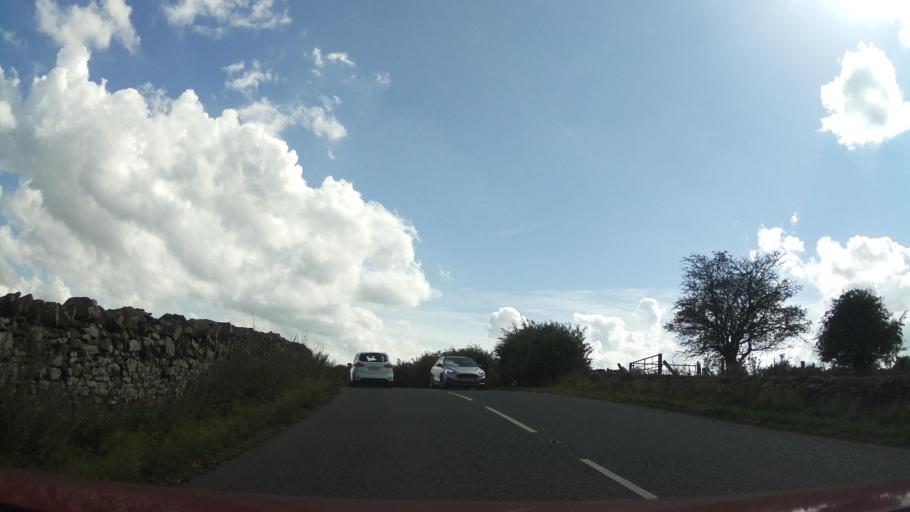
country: GB
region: England
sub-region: North Yorkshire
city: Leyburn
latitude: 54.3258
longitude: -1.8249
